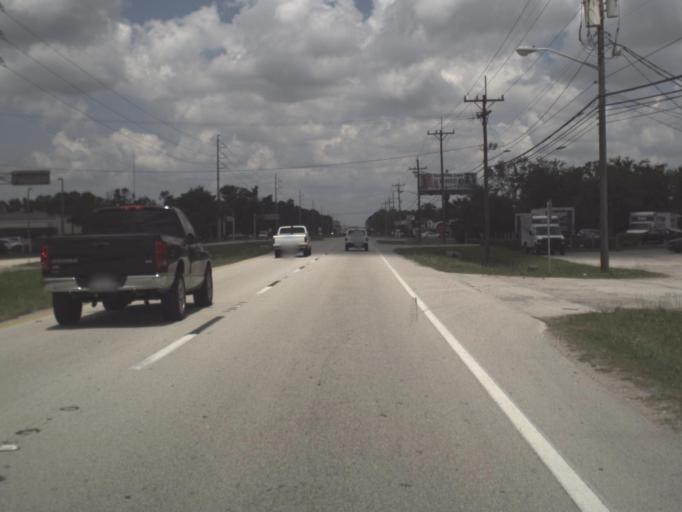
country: US
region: Florida
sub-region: Duval County
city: Jacksonville
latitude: 30.2459
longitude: -81.6016
